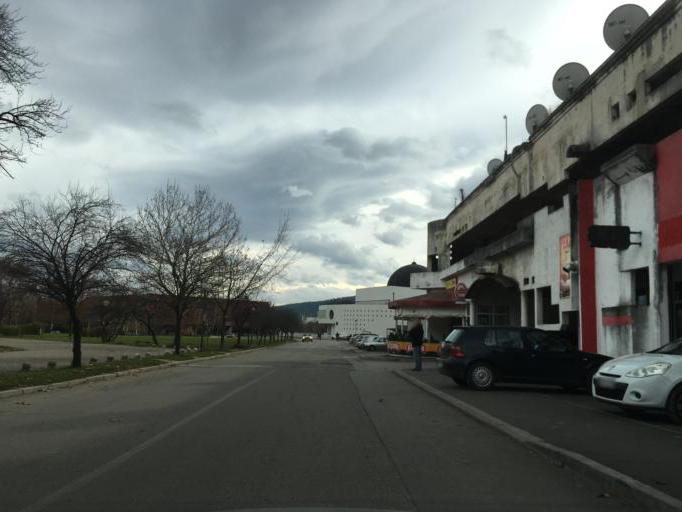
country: BA
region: Federation of Bosnia and Herzegovina
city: Bugojno
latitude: 44.0531
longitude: 17.4443
